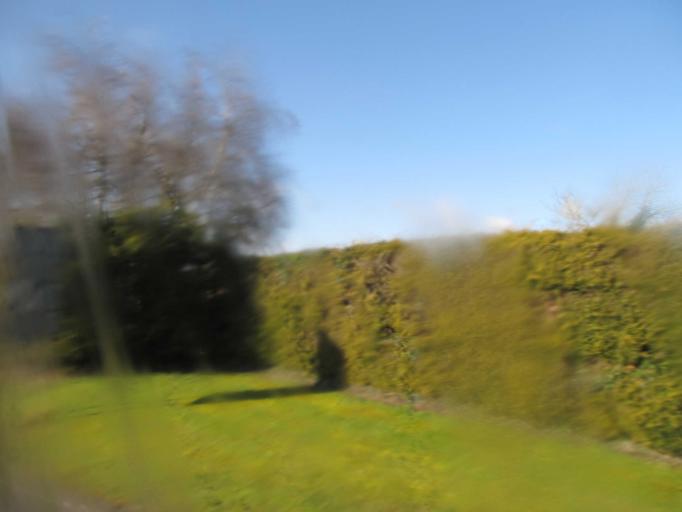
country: GB
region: England
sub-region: Hampshire
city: Kings Worthy
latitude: 51.1485
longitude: -1.3418
